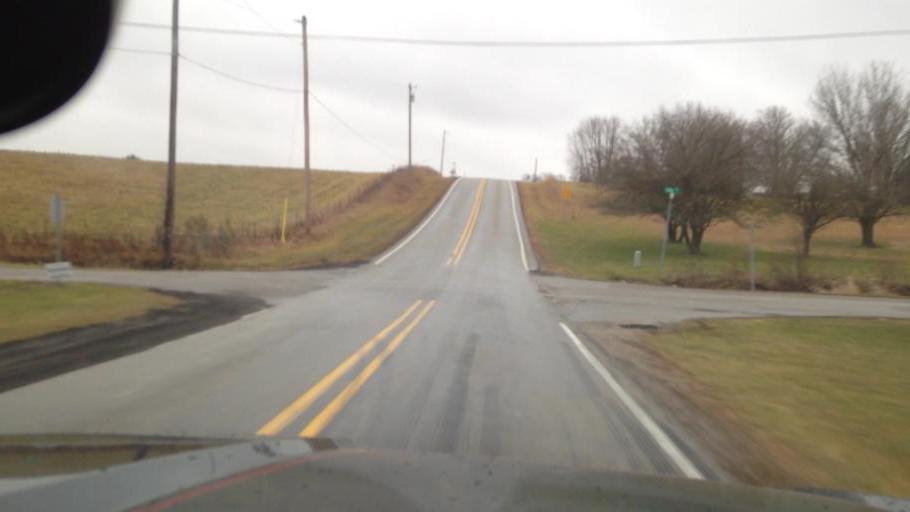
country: US
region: Ohio
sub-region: Preble County
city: New Paris
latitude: 39.9102
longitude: -84.8317
